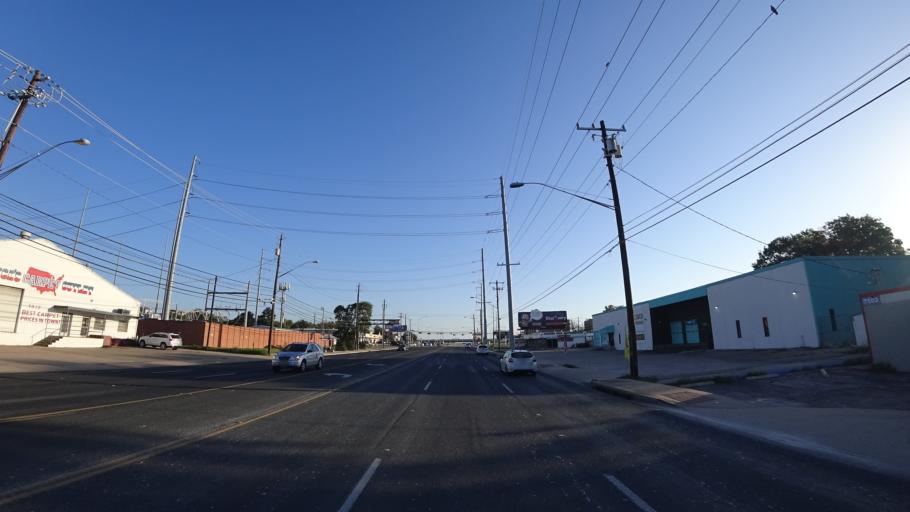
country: US
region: Texas
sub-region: Travis County
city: Austin
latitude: 30.3426
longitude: -97.7158
